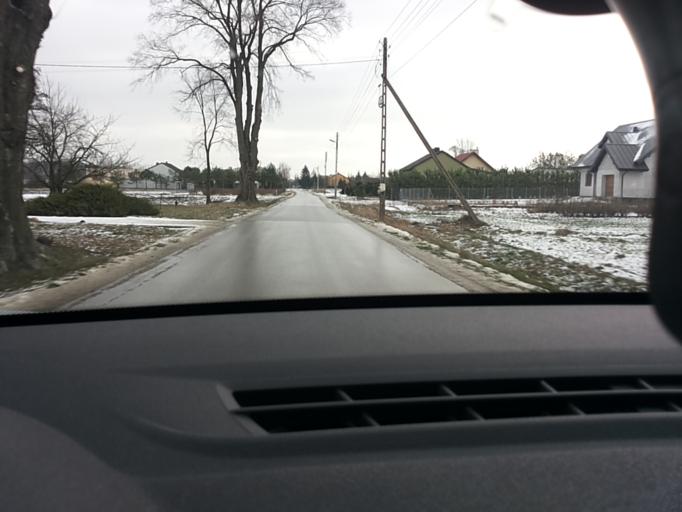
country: PL
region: Lodz Voivodeship
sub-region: Powiat skierniewicki
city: Makow
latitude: 51.9853
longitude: 20.0946
